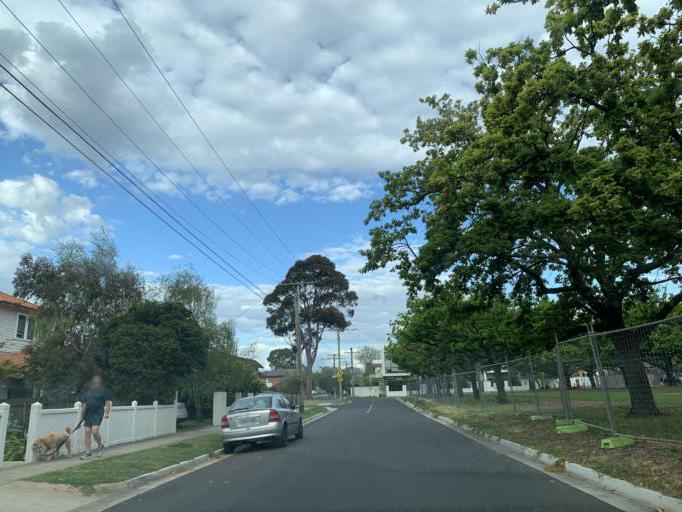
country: AU
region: Victoria
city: Hampton
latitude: -37.9476
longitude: 145.0126
